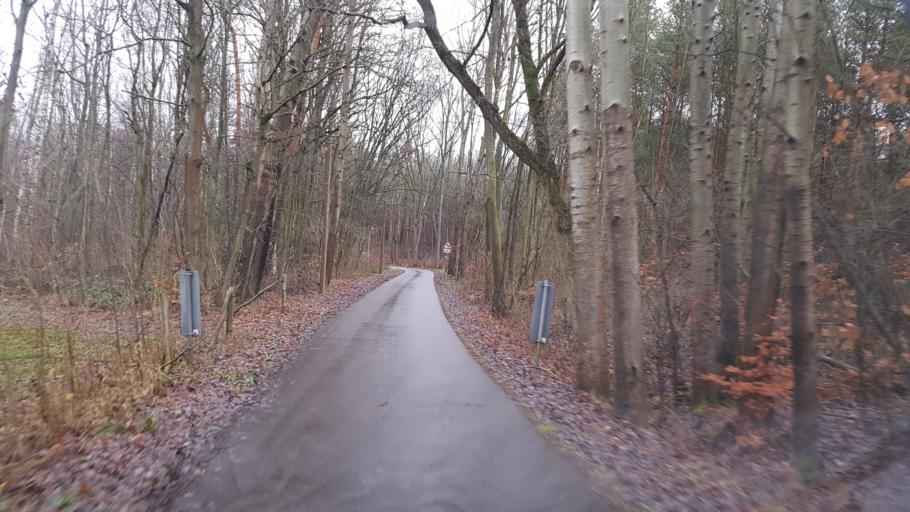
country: DE
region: Brandenburg
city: Altdobern
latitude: 51.6860
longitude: 14.0023
